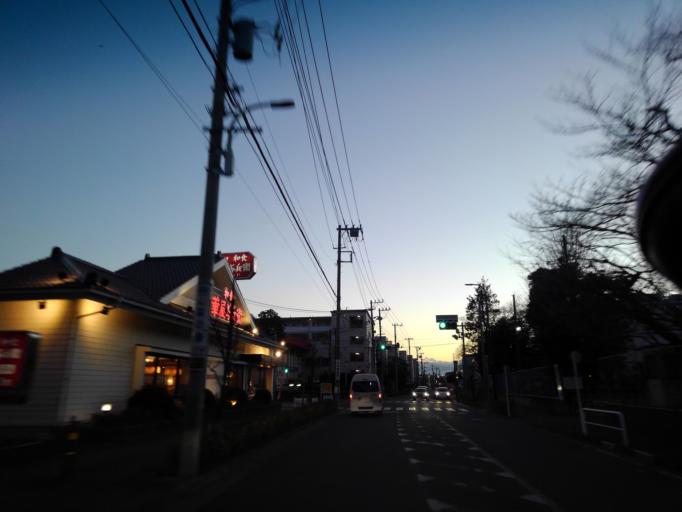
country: JP
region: Tokyo
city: Chofugaoka
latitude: 35.6460
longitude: 139.5680
